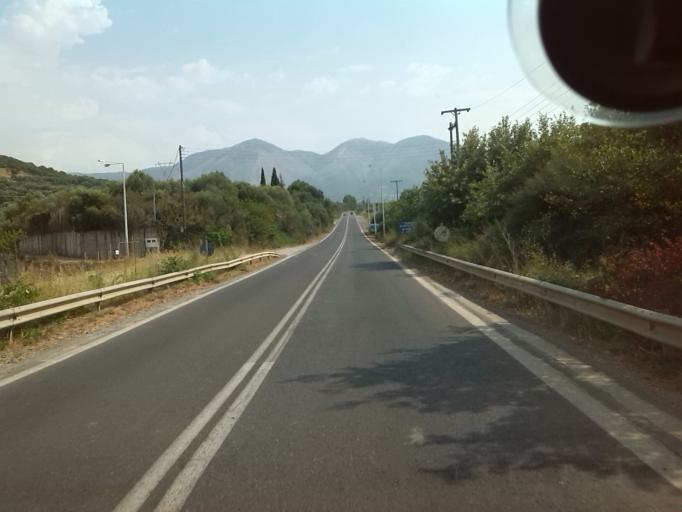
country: GR
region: Peloponnese
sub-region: Nomos Messinias
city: Kyparissia
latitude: 37.2922
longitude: 21.7024
